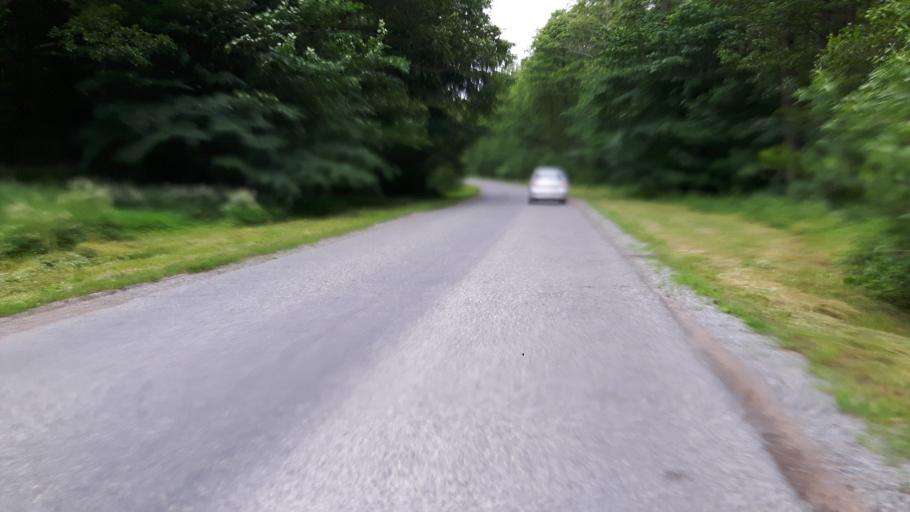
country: LV
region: Liepaja
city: Vec-Liepaja
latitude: 56.5741
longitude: 21.0238
